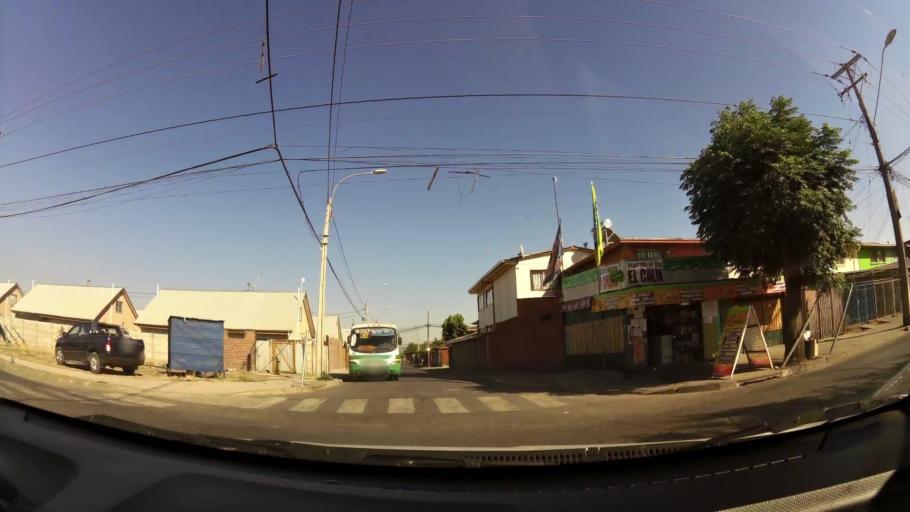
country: CL
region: Maule
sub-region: Provincia de Curico
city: Curico
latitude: -34.9962
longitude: -71.2575
